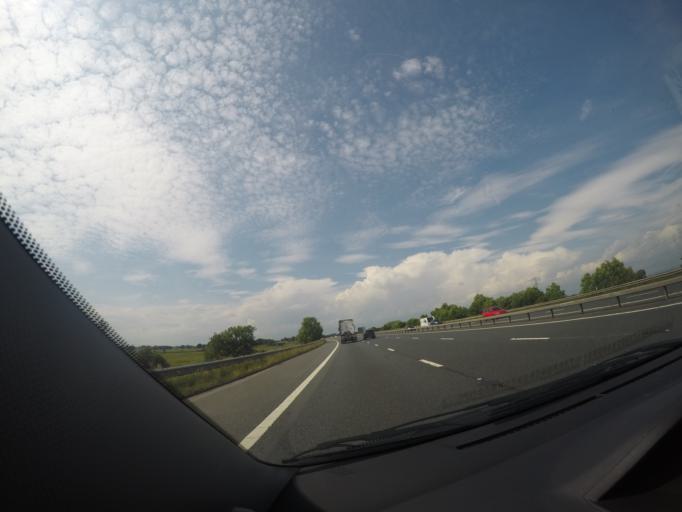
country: GB
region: England
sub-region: Cumbria
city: Scotby
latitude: 54.9051
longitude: -2.8896
